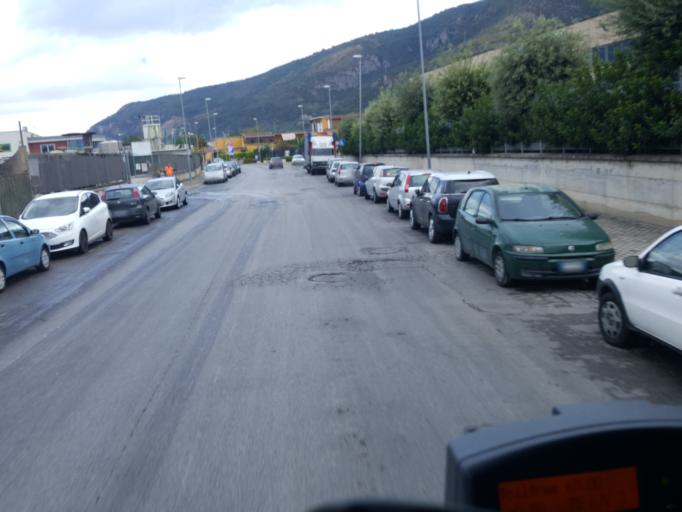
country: IT
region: Campania
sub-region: Provincia di Napoli
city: Striano
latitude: 40.8214
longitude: 14.6000
